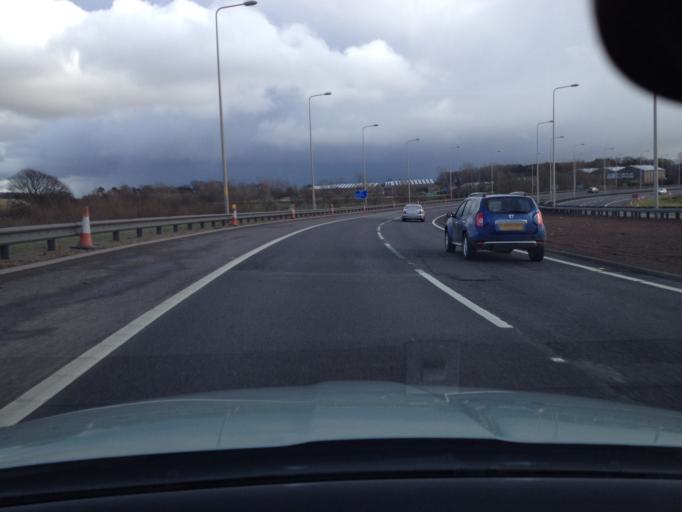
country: GB
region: Scotland
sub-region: Edinburgh
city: Queensferry
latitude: 55.9777
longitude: -3.3815
